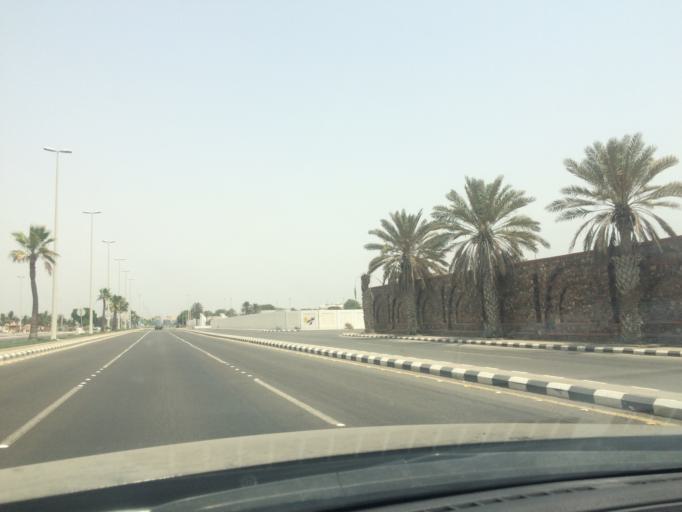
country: SA
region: Makkah
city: Jeddah
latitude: 21.5908
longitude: 39.1149
